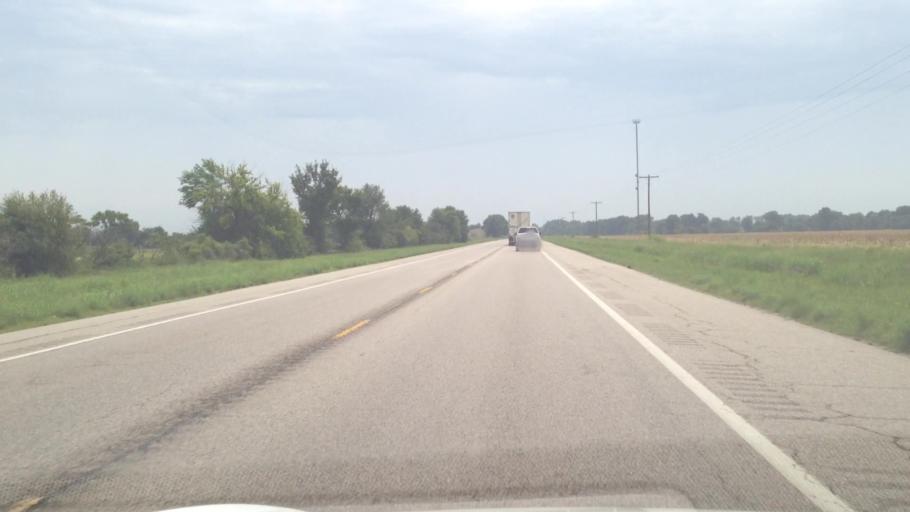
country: US
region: Missouri
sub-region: Jasper County
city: Carl Junction
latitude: 37.2138
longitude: -94.7049
